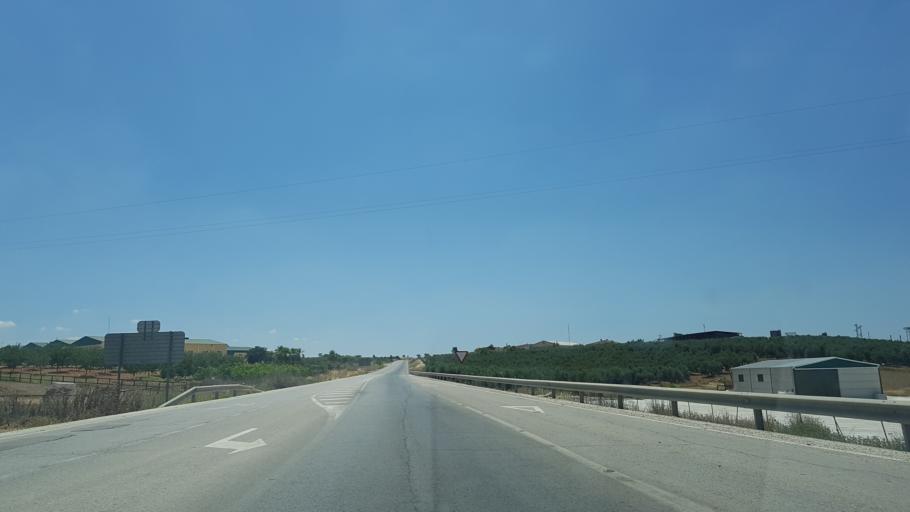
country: ES
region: Andalusia
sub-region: Provincia de Sevilla
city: Herrera
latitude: 37.3629
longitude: -4.8272
